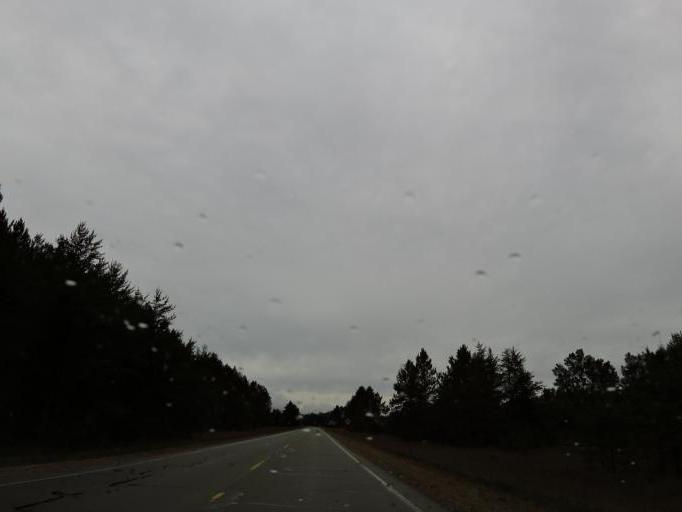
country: US
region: Michigan
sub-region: Roscommon County
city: Roscommon
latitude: 44.4554
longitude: -84.5246
